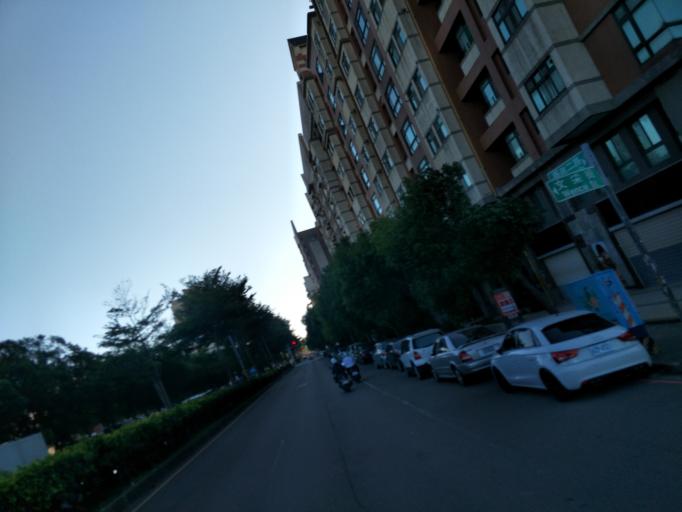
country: TW
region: Taiwan
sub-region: Hsinchu
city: Zhubei
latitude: 24.8350
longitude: 121.0199
